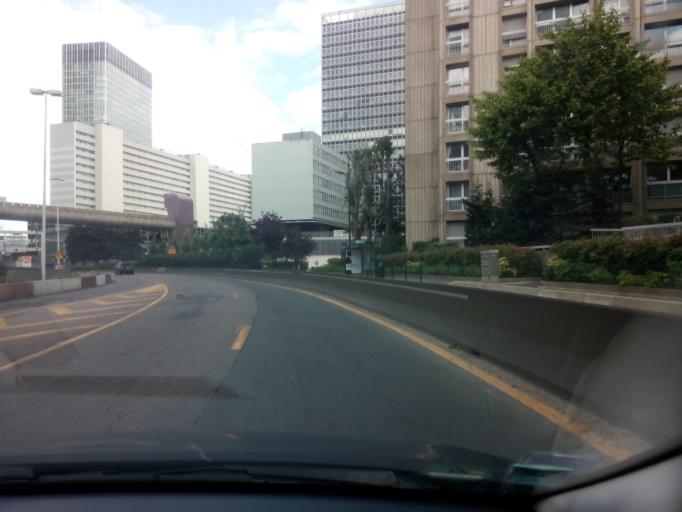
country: FR
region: Ile-de-France
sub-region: Departement des Hauts-de-Seine
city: Puteaux
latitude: 48.8868
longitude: 2.2470
